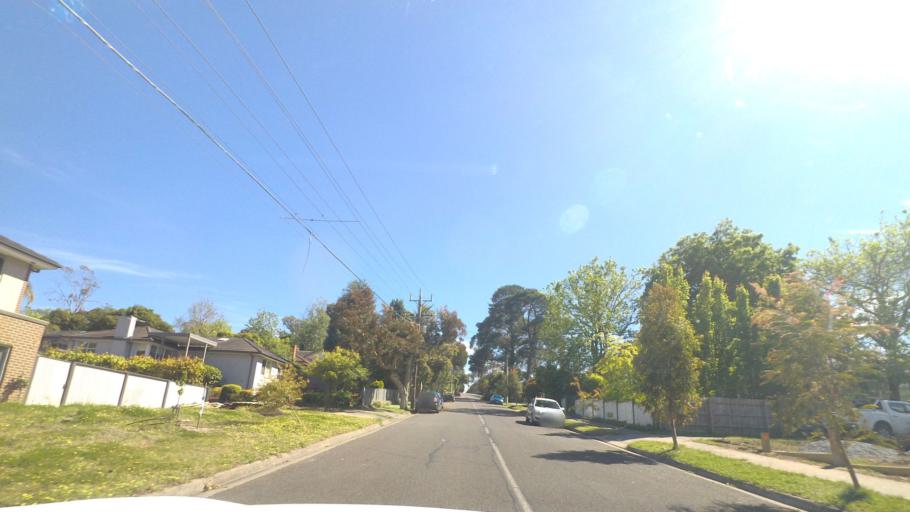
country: AU
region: Victoria
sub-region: Maroondah
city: Ringwood East
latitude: -37.8230
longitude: 145.2579
